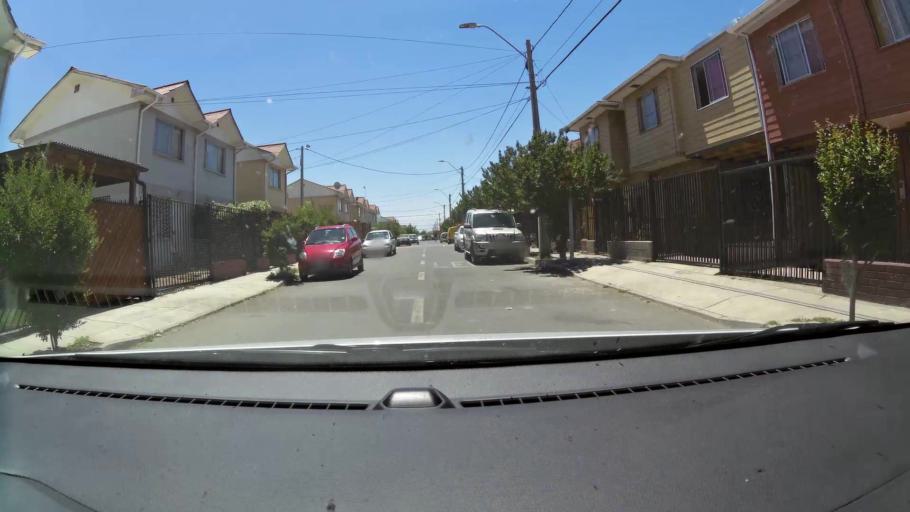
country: CL
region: Santiago Metropolitan
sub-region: Provincia de Maipo
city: San Bernardo
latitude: -33.6046
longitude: -70.6717
